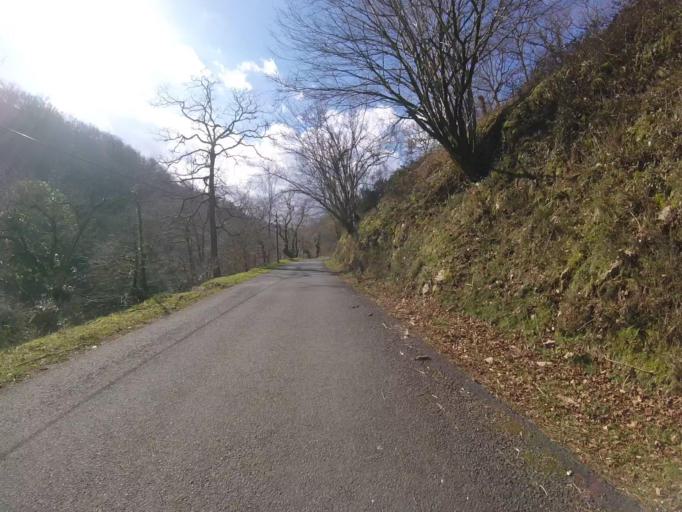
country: ES
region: Navarre
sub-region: Provincia de Navarra
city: Etxalar
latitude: 43.2684
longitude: -1.6043
